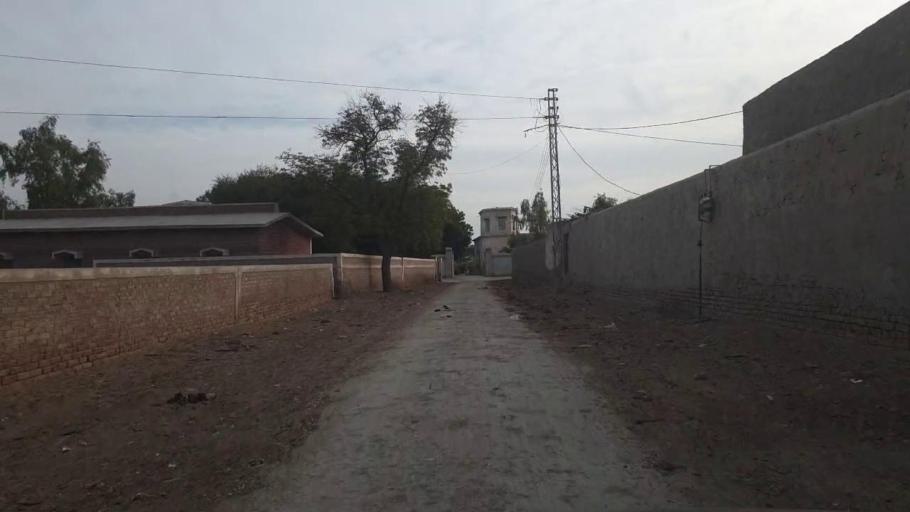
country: PK
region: Sindh
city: Shahpur Chakar
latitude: 26.1324
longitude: 68.6072
